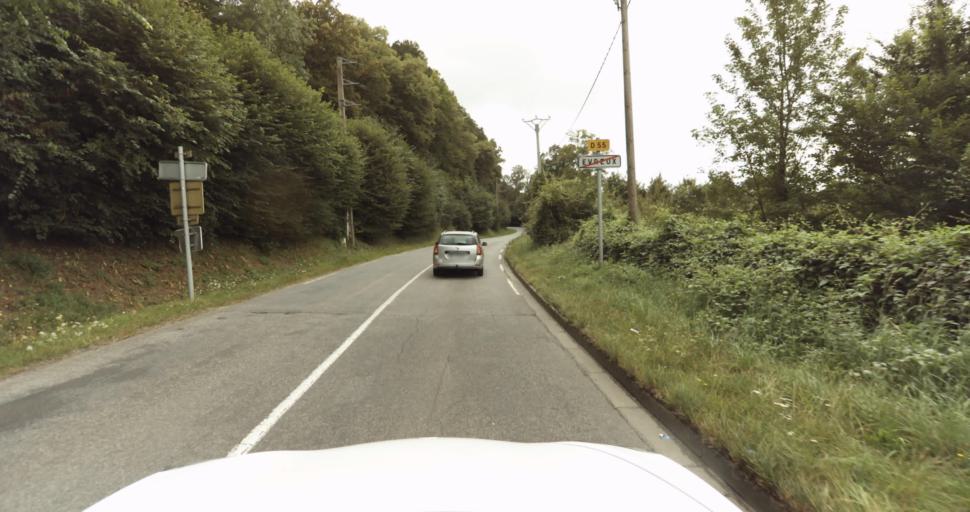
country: FR
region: Haute-Normandie
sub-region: Departement de l'Eure
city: Arnieres-sur-Iton
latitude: 49.0085
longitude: 1.1161
